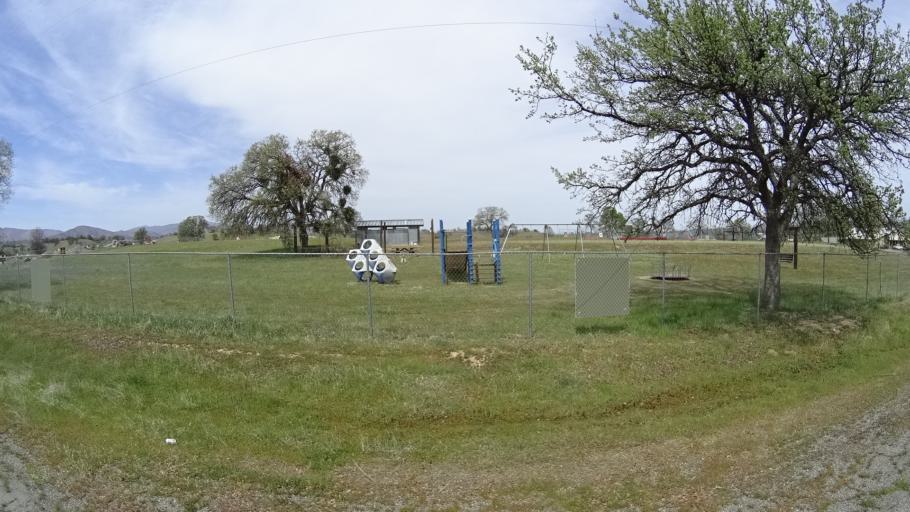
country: US
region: California
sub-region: Glenn County
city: Willows
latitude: 39.6064
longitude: -122.5432
